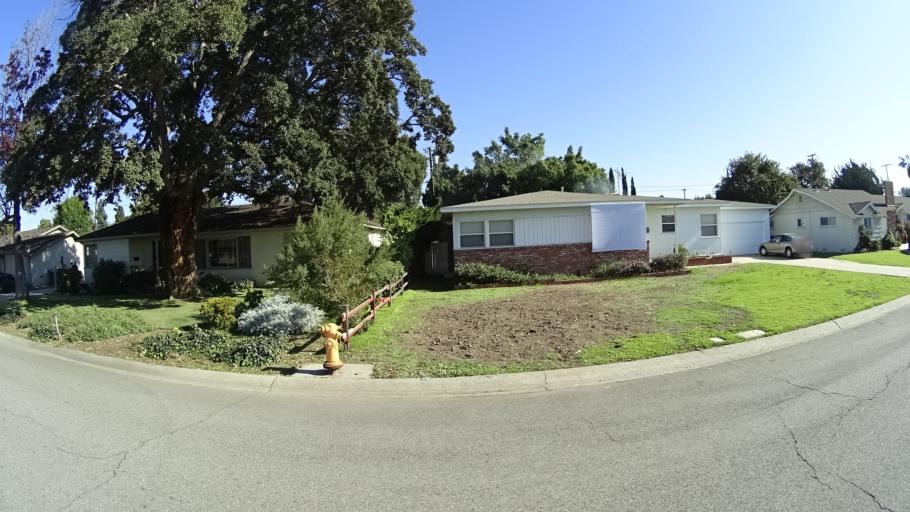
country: US
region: California
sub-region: Orange County
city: Garden Grove
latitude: 33.7870
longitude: -117.9336
